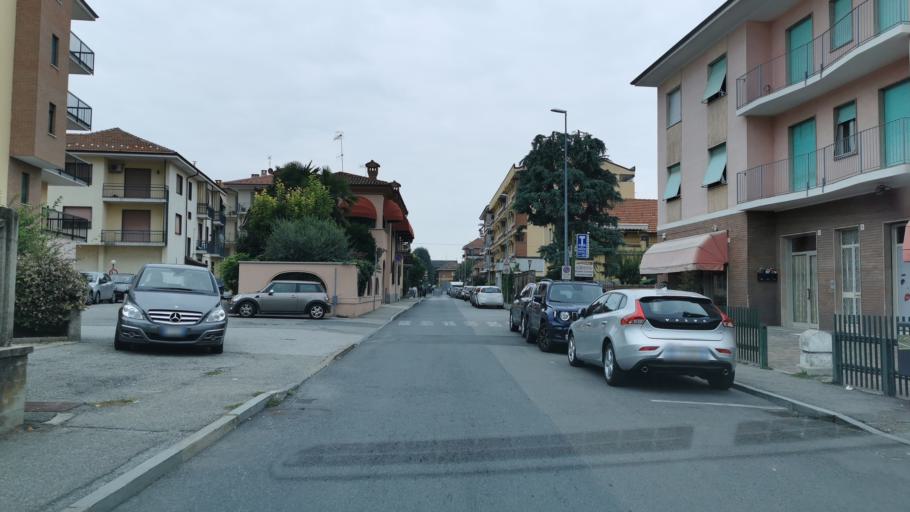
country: IT
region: Piedmont
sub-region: Provincia di Cuneo
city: Bra
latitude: 44.6928
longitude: 7.8585
